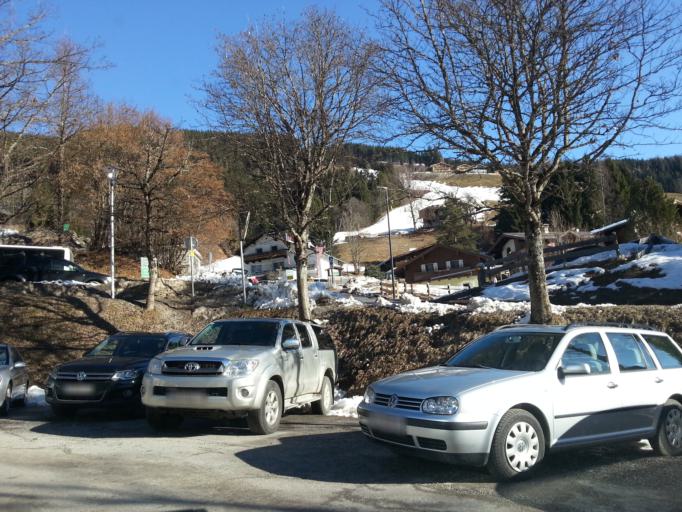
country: AT
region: Salzburg
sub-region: Politischer Bezirk Zell am See
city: Zell am See
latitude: 47.3266
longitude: 12.7732
